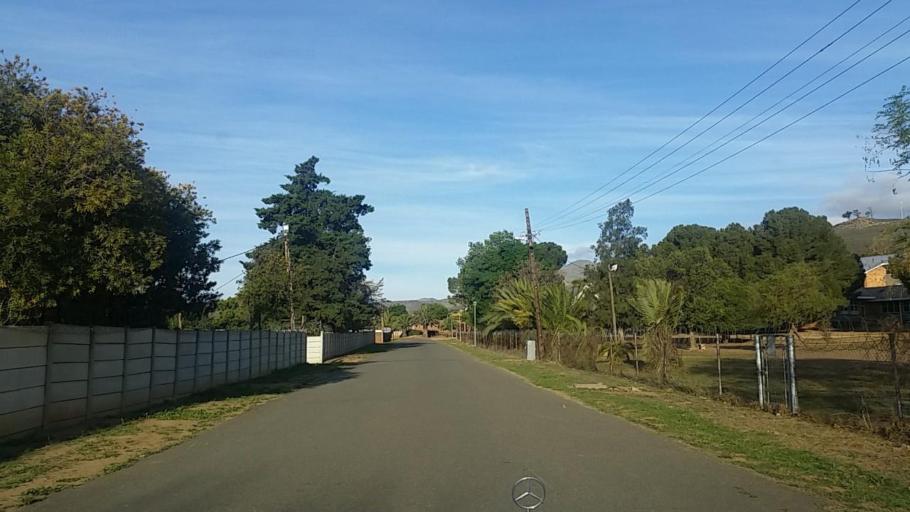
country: ZA
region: Western Cape
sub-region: Eden District Municipality
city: Knysna
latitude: -33.6560
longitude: 23.1231
